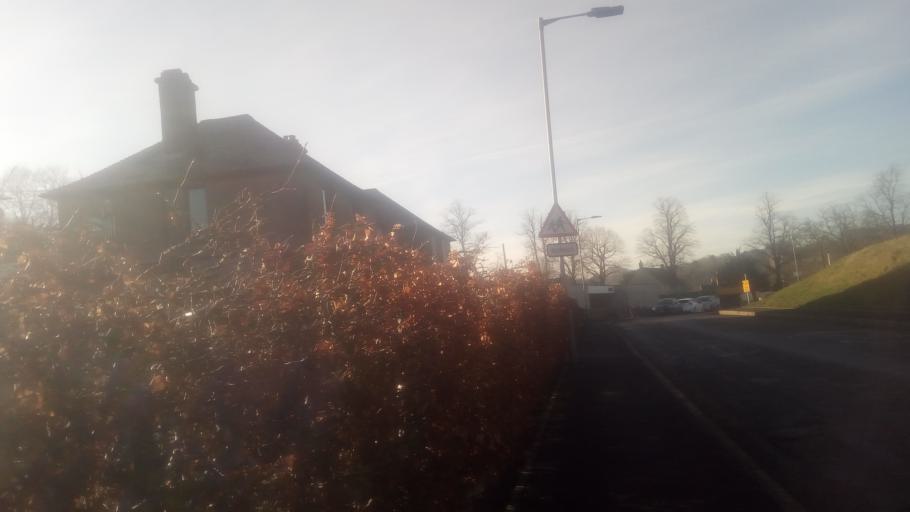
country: GB
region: Scotland
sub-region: The Scottish Borders
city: Jedburgh
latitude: 55.4799
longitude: -2.5485
